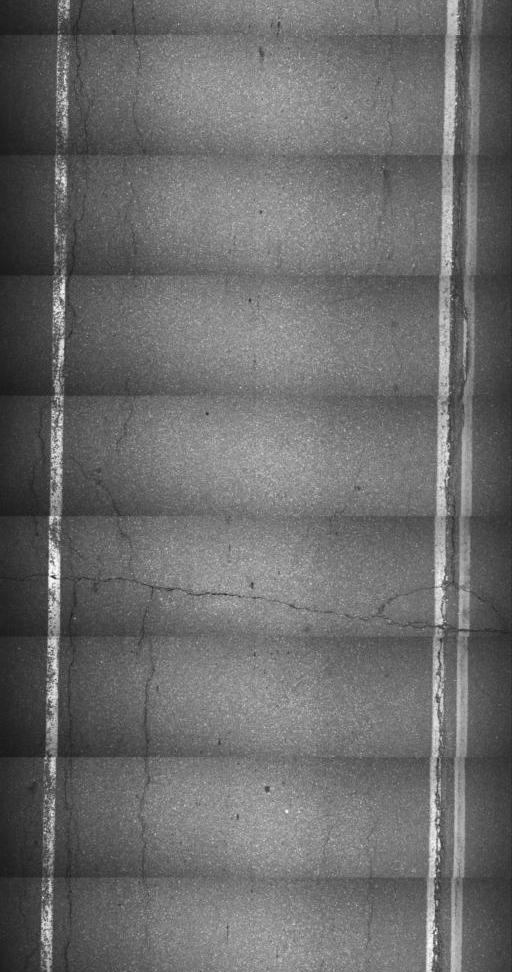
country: US
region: New Hampshire
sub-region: Coos County
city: Colebrook
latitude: 45.0090
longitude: -71.5629
